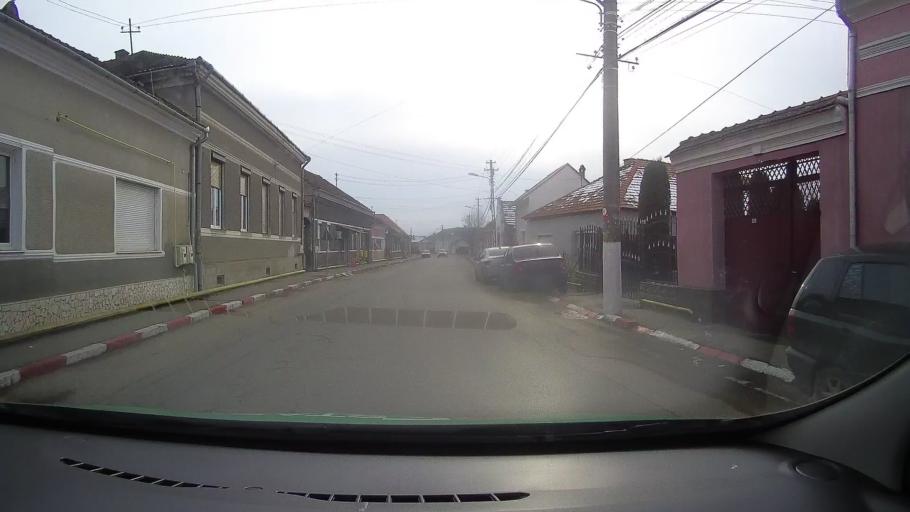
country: RO
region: Hunedoara
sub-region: Comuna Geoagiu
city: Geoagiu
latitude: 45.9237
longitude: 23.1995
